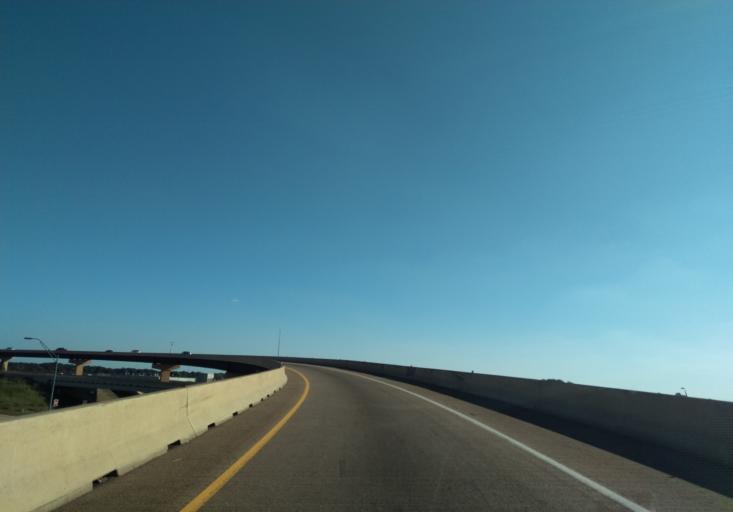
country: US
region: Texas
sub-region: Waller County
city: Hempstead
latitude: 30.1158
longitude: -96.0761
